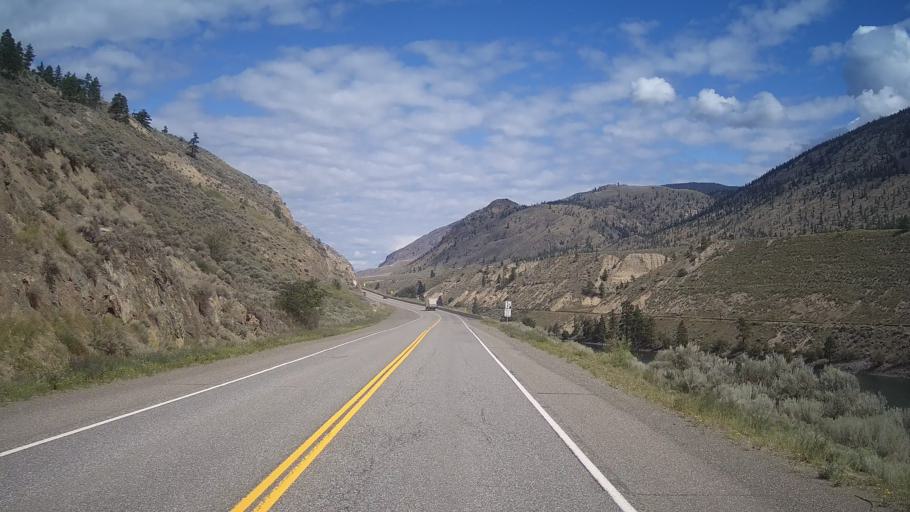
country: CA
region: British Columbia
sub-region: Thompson-Nicola Regional District
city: Ashcroft
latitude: 50.5323
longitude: -121.2857
